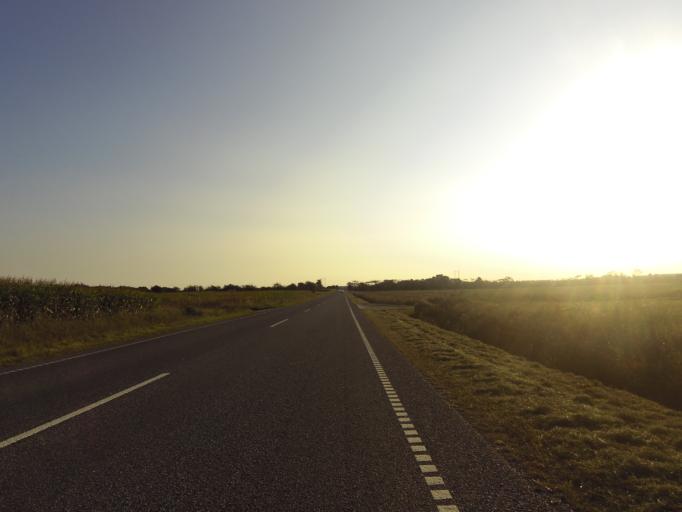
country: DK
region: South Denmark
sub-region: Vejen Kommune
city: Vejen
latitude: 55.4094
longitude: 9.1282
